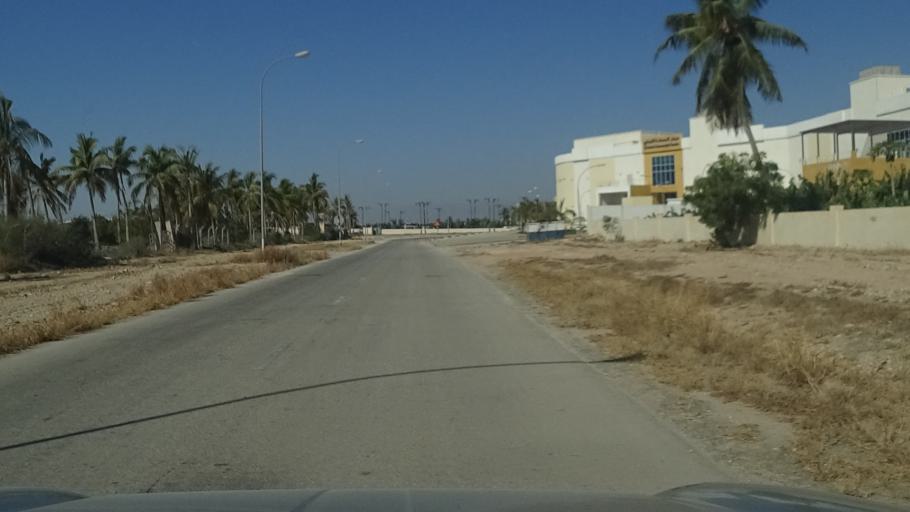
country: OM
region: Zufar
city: Salalah
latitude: 17.0345
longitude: 54.1495
